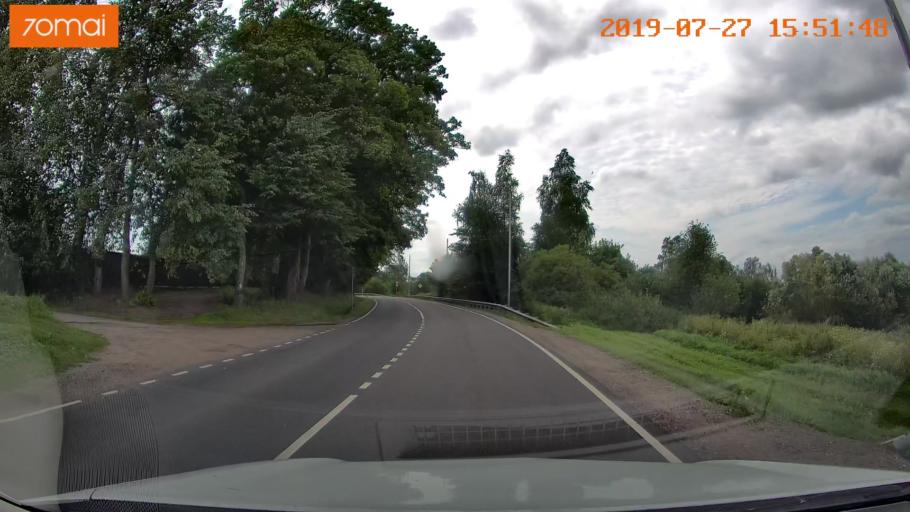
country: RU
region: Kaliningrad
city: Chernyakhovsk
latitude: 54.6026
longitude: 21.9732
